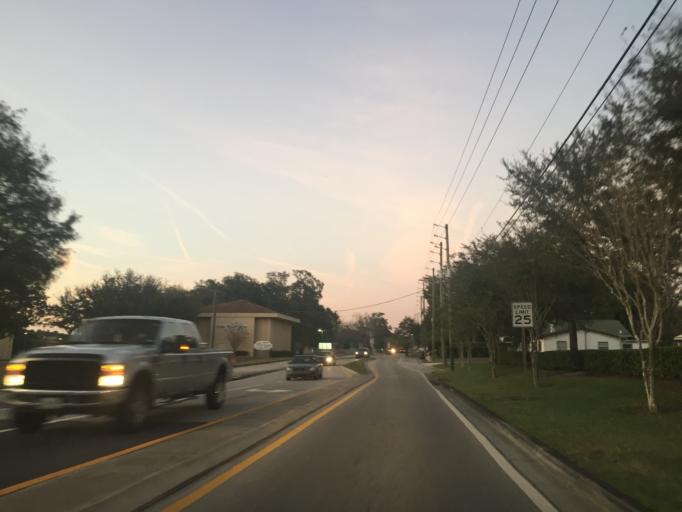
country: US
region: Florida
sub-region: Seminole County
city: Oviedo
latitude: 28.6704
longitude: -81.2043
